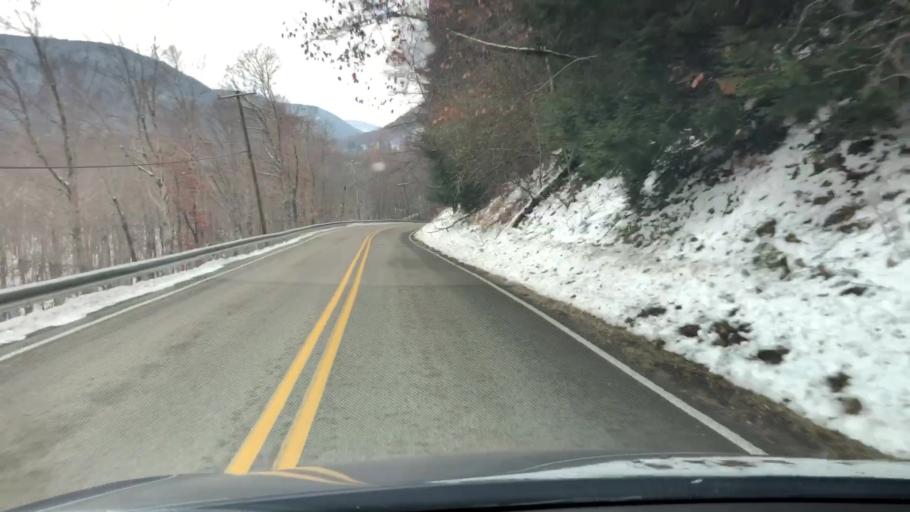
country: US
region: Pennsylvania
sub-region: Elk County
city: Saint Marys
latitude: 41.2946
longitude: -78.3933
